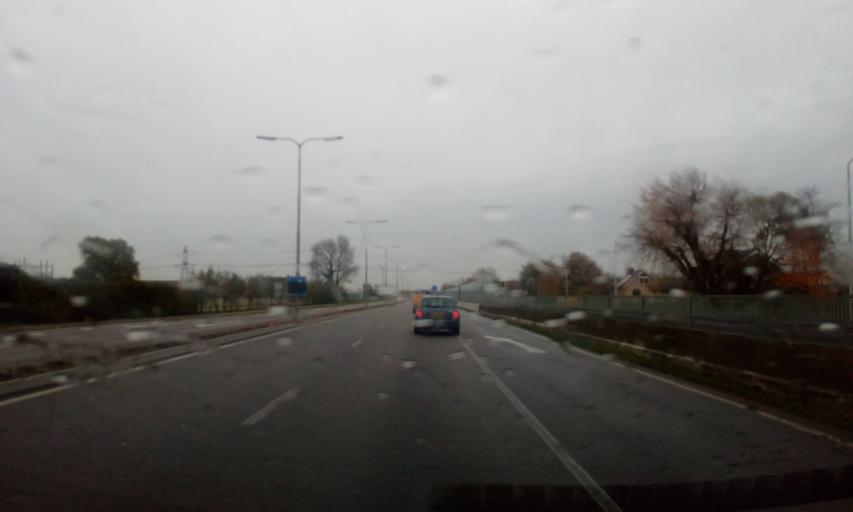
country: NL
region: South Holland
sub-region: Gemeente Westland
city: Naaldwijk
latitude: 51.9882
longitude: 4.2211
